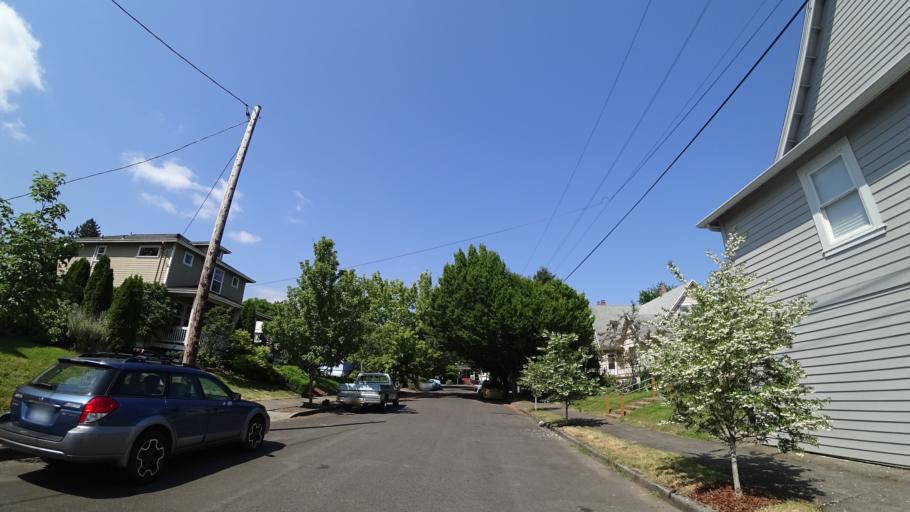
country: US
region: Oregon
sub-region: Multnomah County
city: Portland
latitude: 45.5690
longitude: -122.6551
